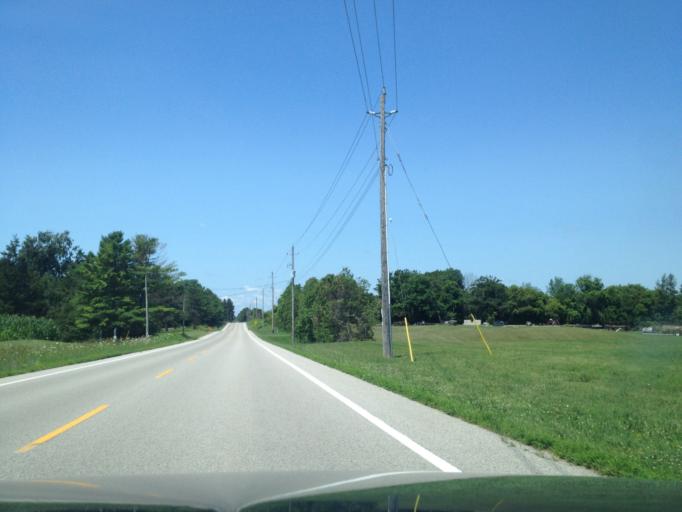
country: CA
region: Ontario
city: Norfolk County
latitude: 42.5915
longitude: -80.6346
